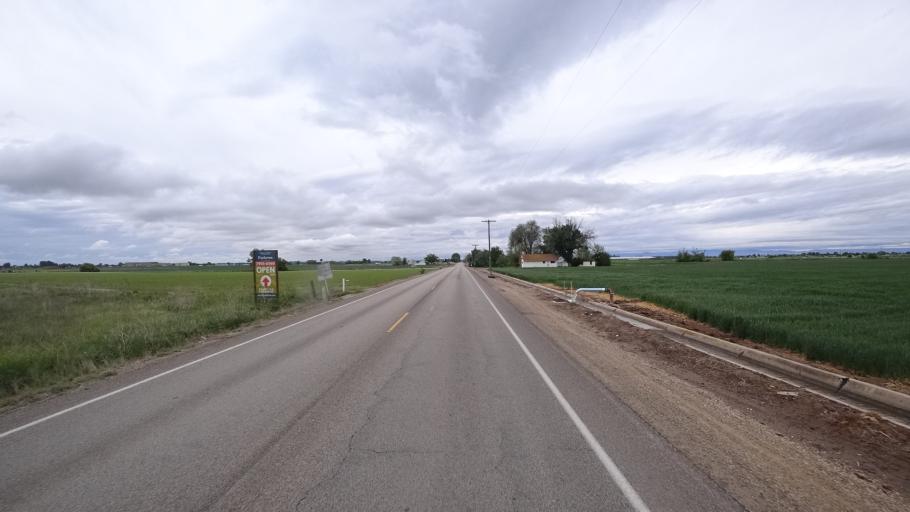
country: US
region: Idaho
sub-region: Ada County
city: Star
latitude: 43.6475
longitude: -116.4936
